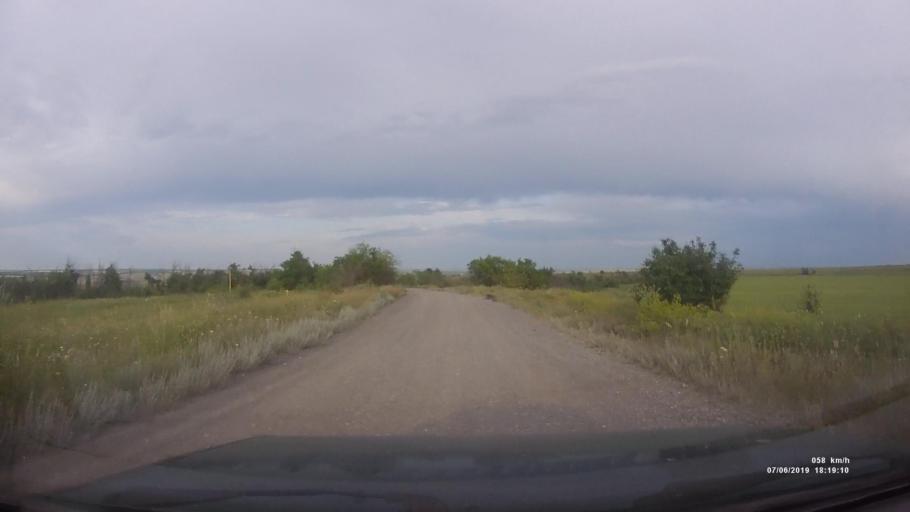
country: RU
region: Rostov
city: Staraya Stanitsa
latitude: 48.2558
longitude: 40.3700
